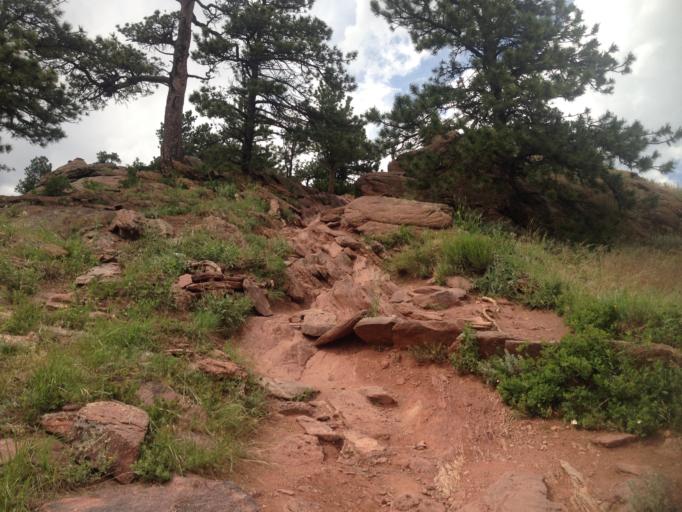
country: US
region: Colorado
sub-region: Boulder County
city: Boulder
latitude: 40.0323
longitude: -105.3044
